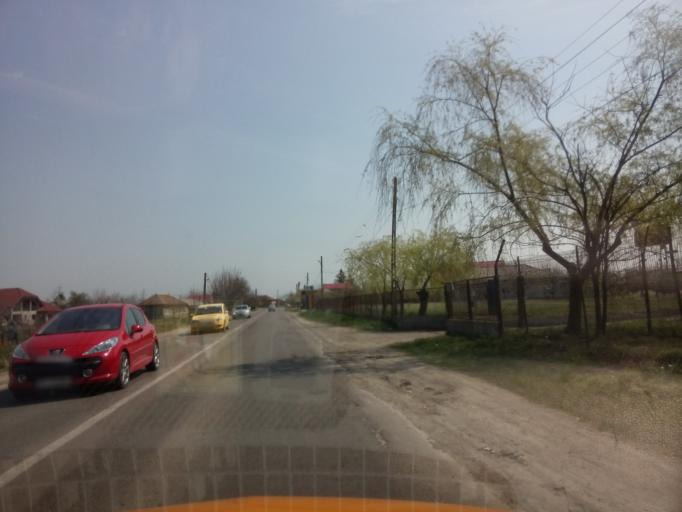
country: RO
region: Calarasi
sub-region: Comuna Soldanu
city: Negoesti
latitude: 44.2310
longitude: 26.4917
